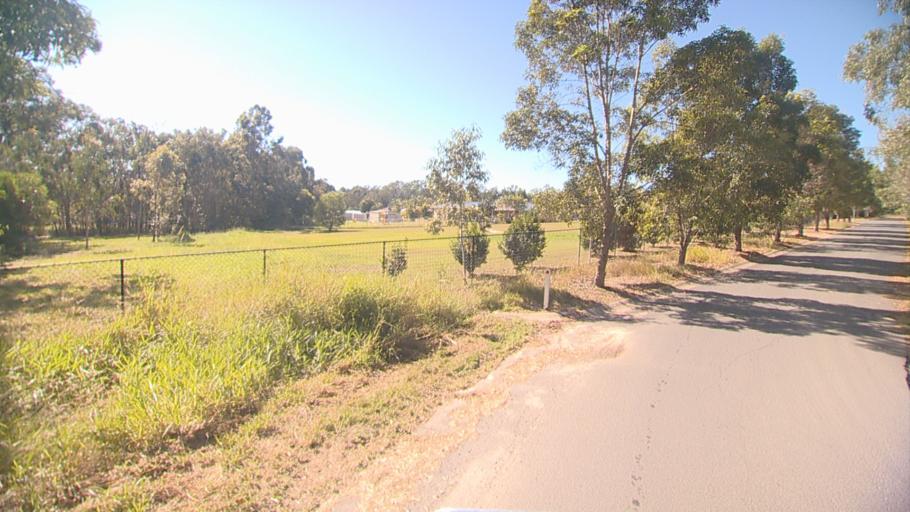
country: AU
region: Queensland
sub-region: Logan
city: Park Ridge South
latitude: -27.6873
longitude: 153.0062
